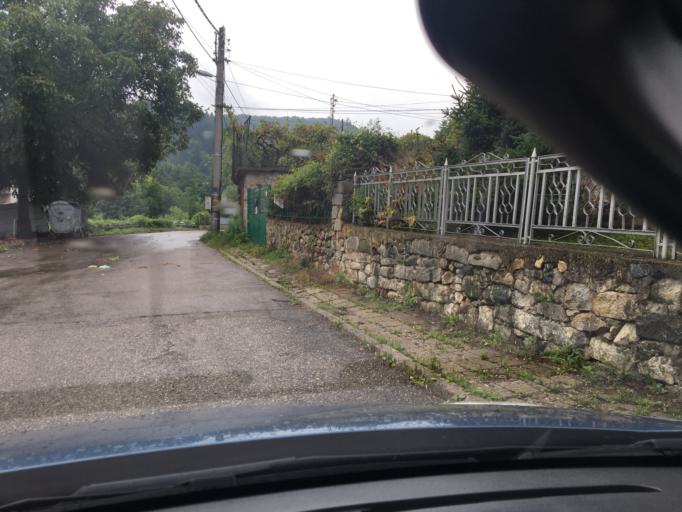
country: BG
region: Sofia-Capital
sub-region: Stolichna Obshtina
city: Sofia
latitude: 42.5908
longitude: 23.4091
